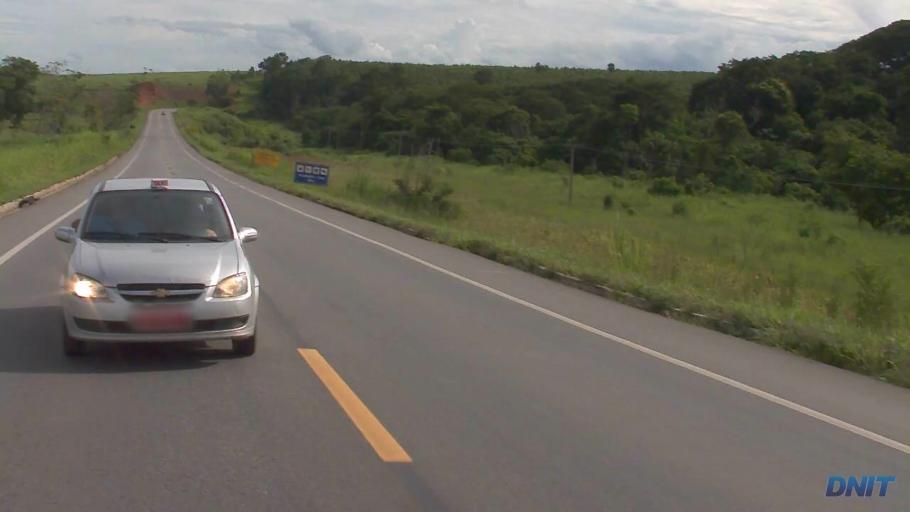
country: BR
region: Minas Gerais
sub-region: Belo Oriente
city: Belo Oriente
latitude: -19.2596
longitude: -42.3428
